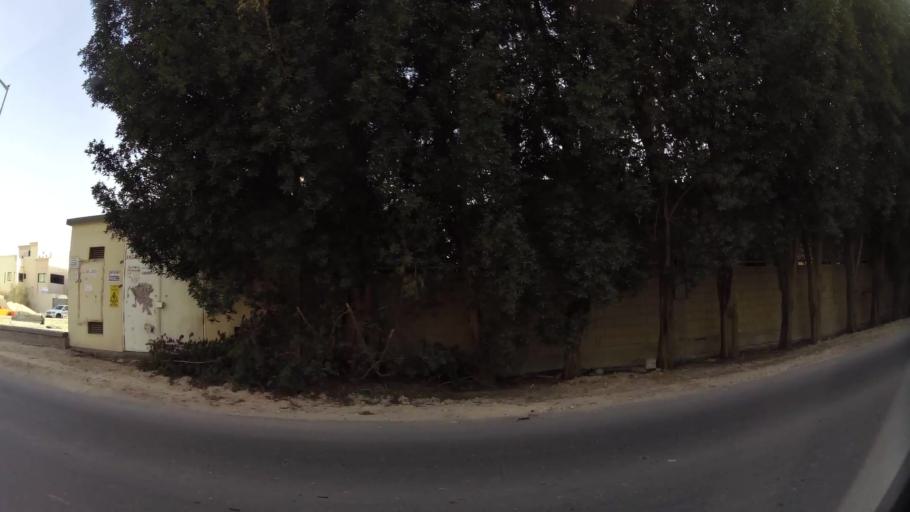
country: BH
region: Manama
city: Jidd Hafs
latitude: 26.2033
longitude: 50.4955
